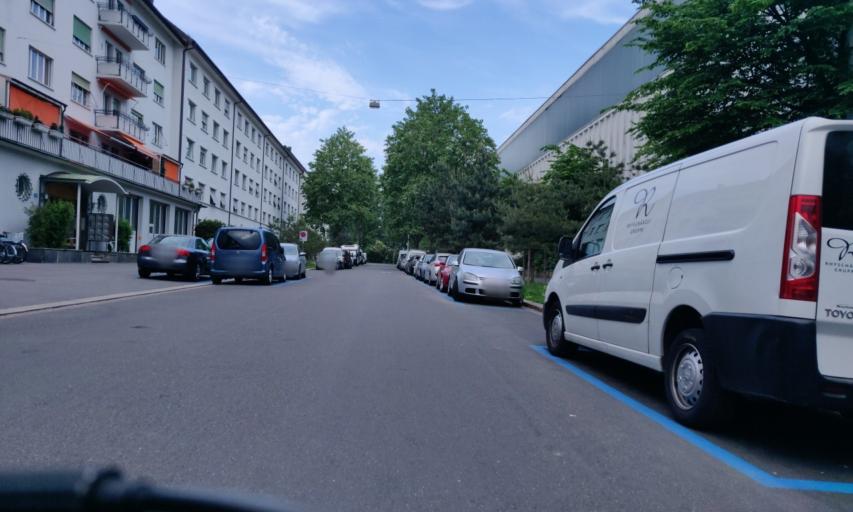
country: FR
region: Alsace
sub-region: Departement du Haut-Rhin
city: Village-Neuf
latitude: 47.5775
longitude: 7.5930
